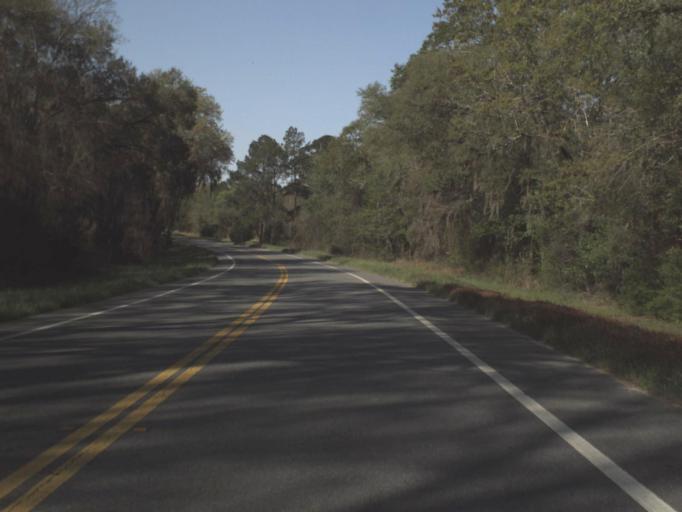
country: US
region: Florida
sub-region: Jackson County
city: Malone
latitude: 30.9627
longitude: -85.1227
